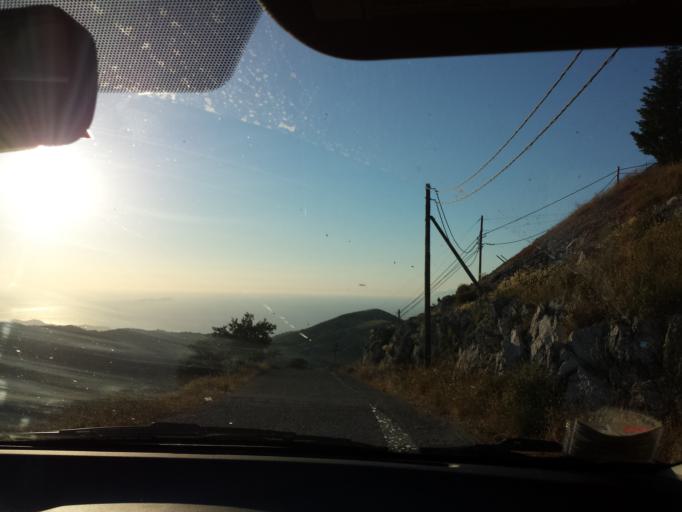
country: GR
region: Ionian Islands
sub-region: Nomos Kerkyras
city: Acharavi
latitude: 39.7475
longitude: 19.8719
